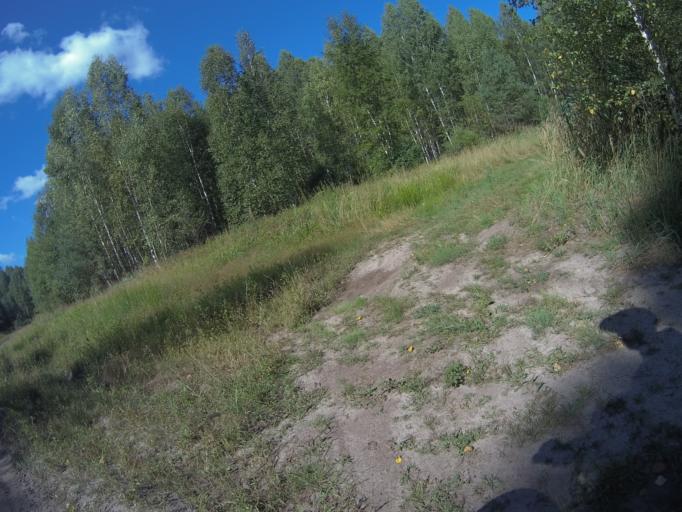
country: RU
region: Vladimir
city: Raduzhnyy
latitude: 55.9256
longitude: 40.2377
